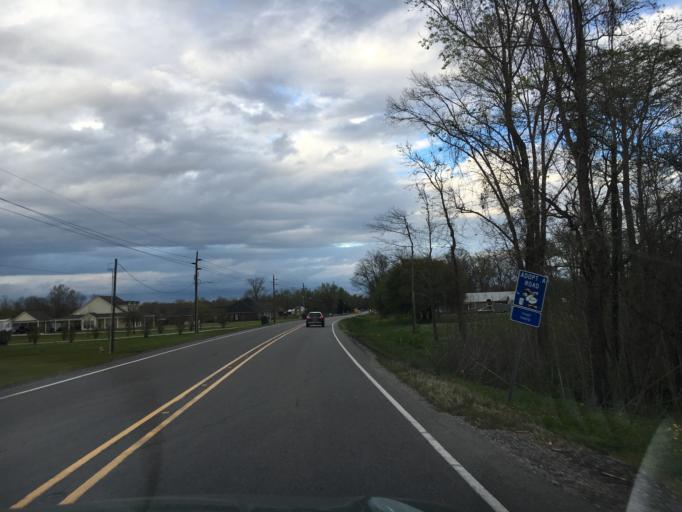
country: US
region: Louisiana
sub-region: West Baton Rouge Parish
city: Erwinville
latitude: 30.4761
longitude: -91.3912
